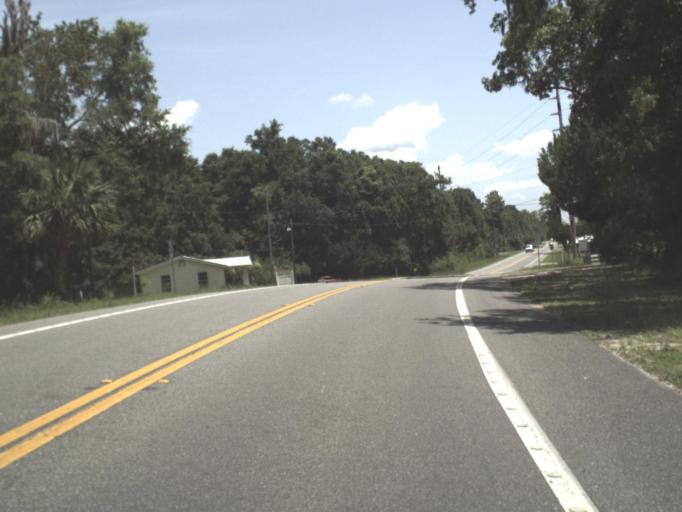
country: US
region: Florida
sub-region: Taylor County
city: Steinhatchee
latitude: 29.6753
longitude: -83.3694
